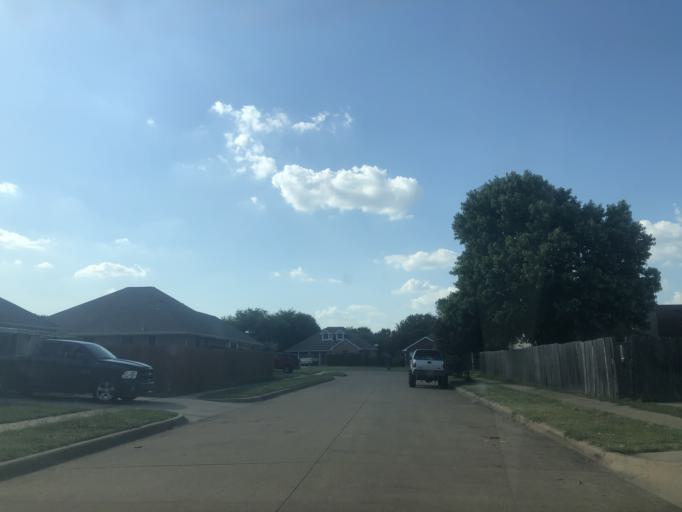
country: US
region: Texas
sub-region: Tarrant County
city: Saginaw
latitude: 32.8536
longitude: -97.3866
